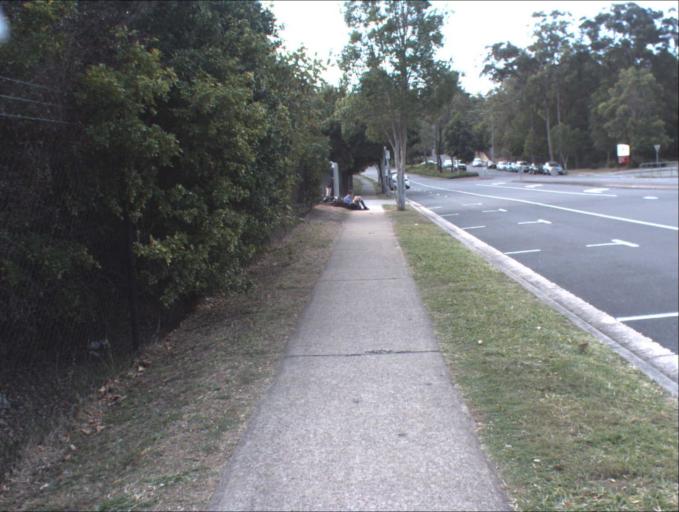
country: AU
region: Queensland
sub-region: Logan
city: Slacks Creek
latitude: -27.6344
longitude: 153.1484
